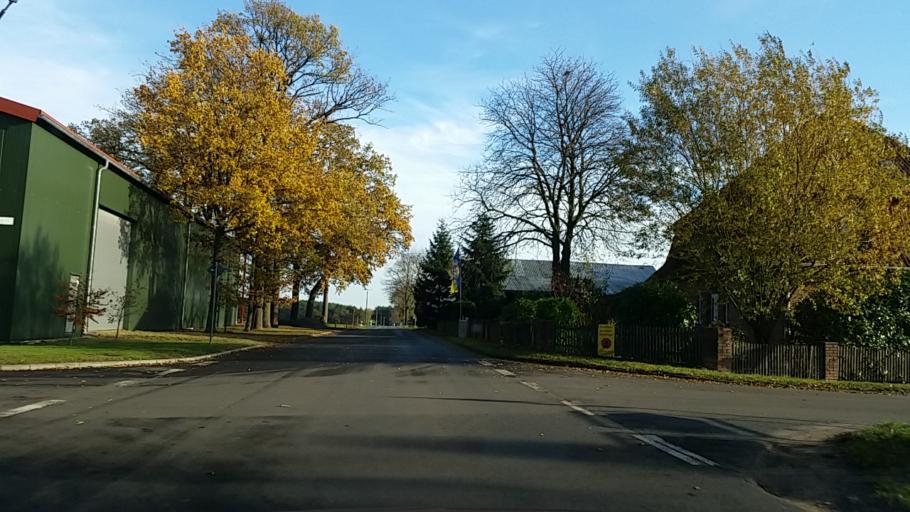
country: DE
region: Lower Saxony
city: Dedelstorf
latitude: 52.6768
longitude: 10.5401
